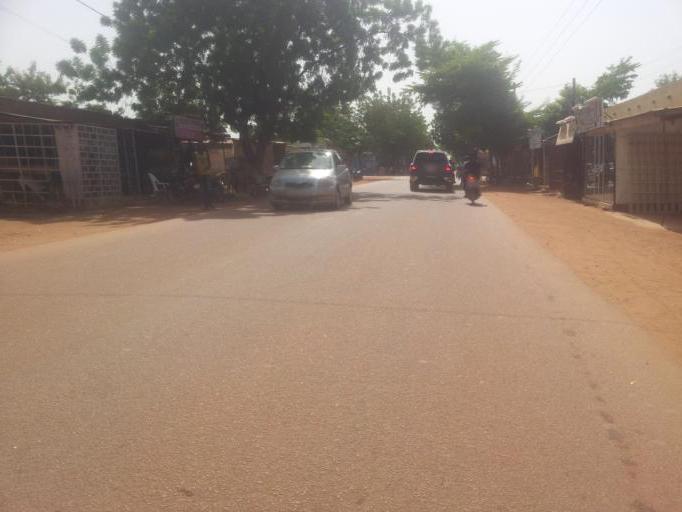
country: BF
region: Centre
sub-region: Kadiogo Province
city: Ouagadougou
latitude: 12.3806
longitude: -1.5410
